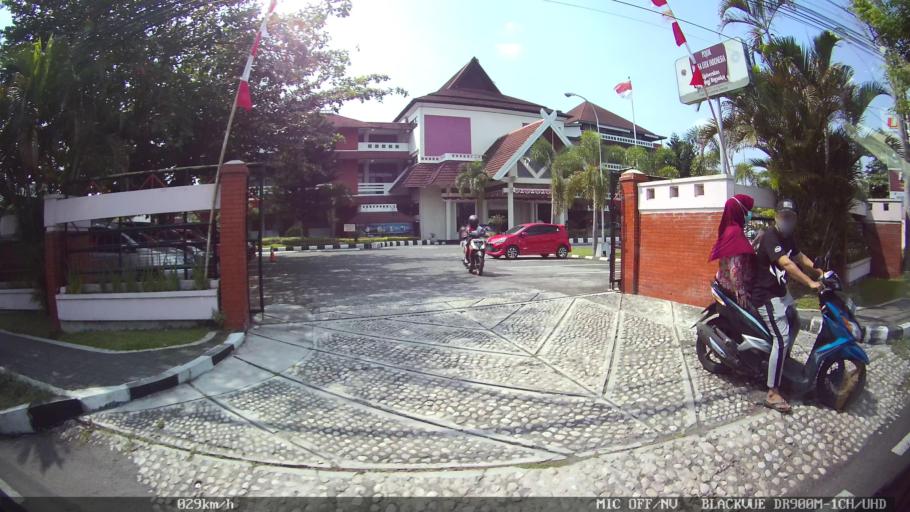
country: ID
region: Daerah Istimewa Yogyakarta
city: Yogyakarta
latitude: -7.8057
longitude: 110.3884
